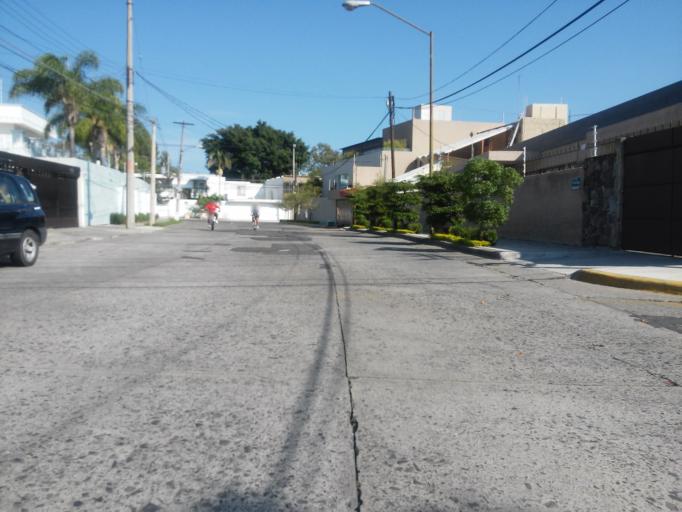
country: MX
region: Jalisco
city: Guadalajara
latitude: 20.6624
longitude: -103.3872
